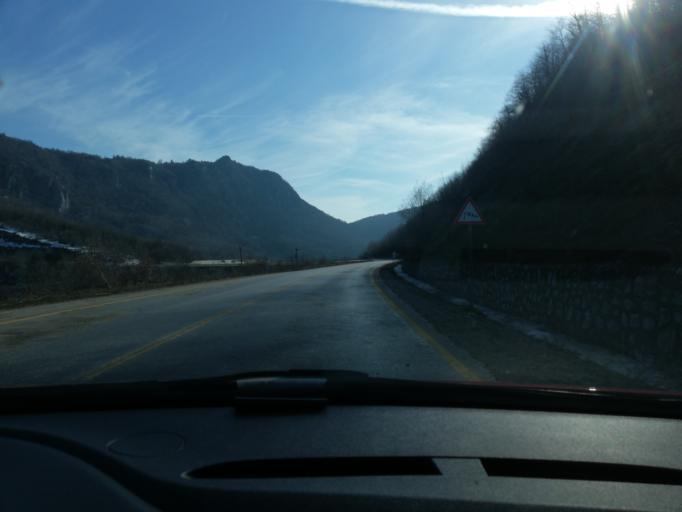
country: TR
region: Kastamonu
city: Cide
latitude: 41.8639
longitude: 33.0529
